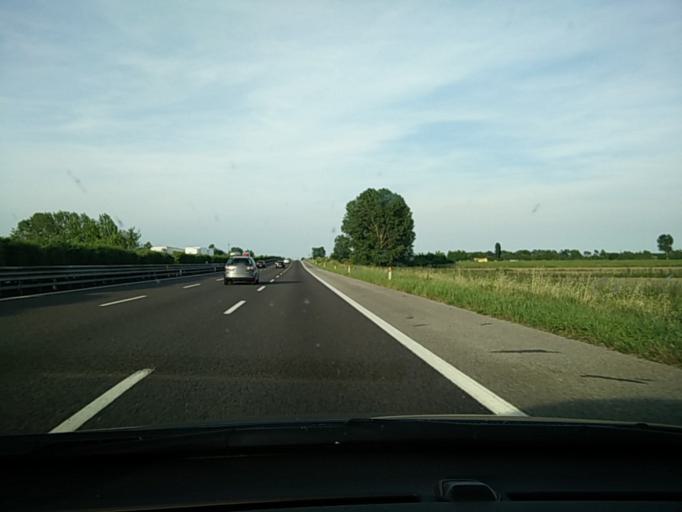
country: IT
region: Veneto
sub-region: Provincia di Venezia
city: Fiesso d'Artico
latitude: 45.4346
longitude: 12.0180
